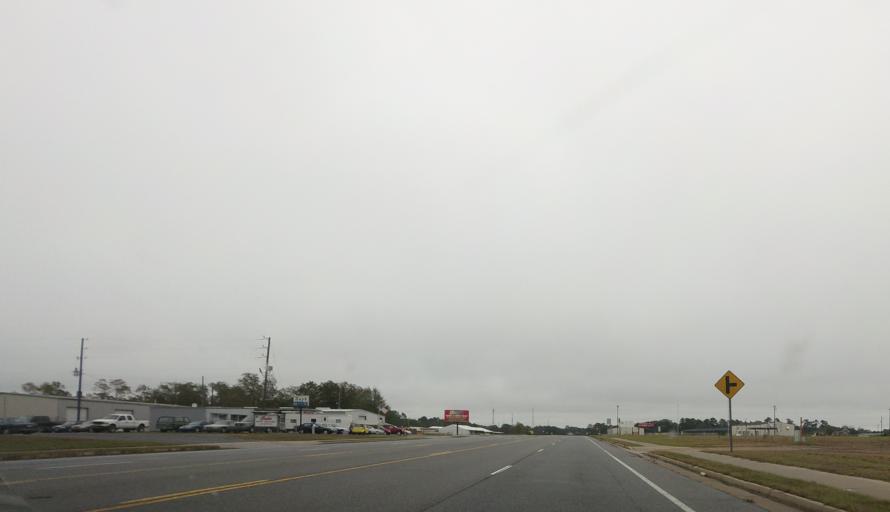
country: US
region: Georgia
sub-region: Taylor County
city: Reynolds
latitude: 32.5617
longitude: -84.1110
